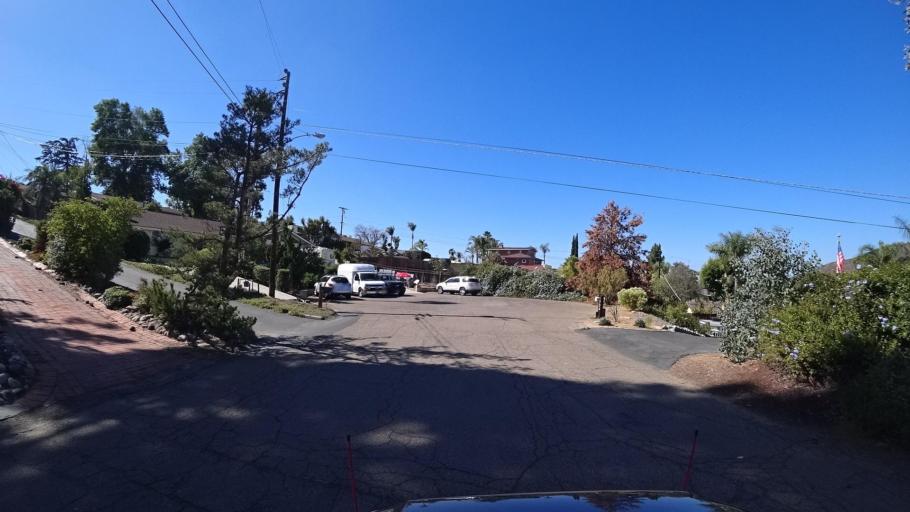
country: US
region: California
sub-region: San Diego County
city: Winter Gardens
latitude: 32.8185
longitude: -116.9245
